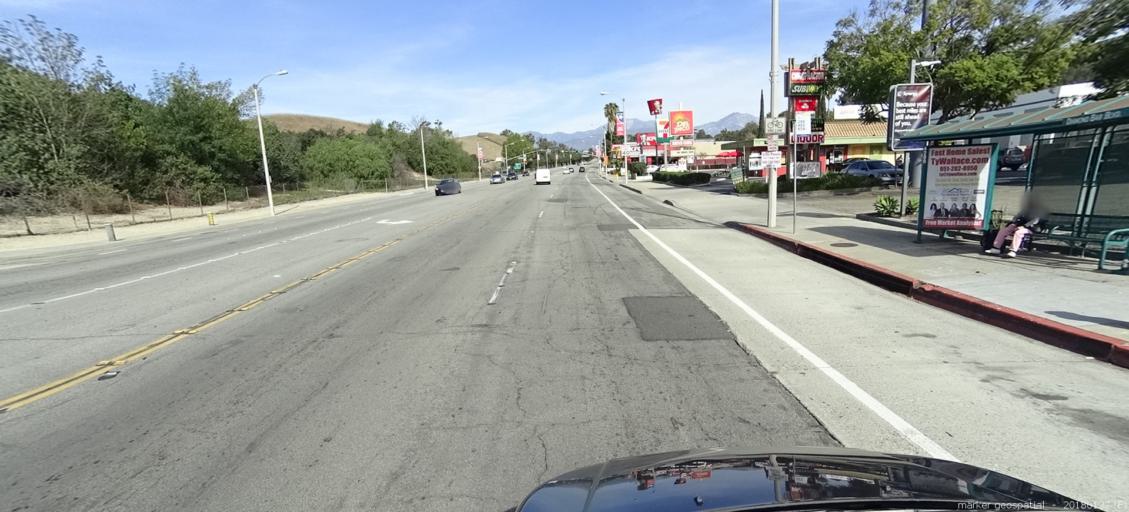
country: US
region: California
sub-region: Los Angeles County
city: Diamond Bar
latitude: 34.0289
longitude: -117.8105
